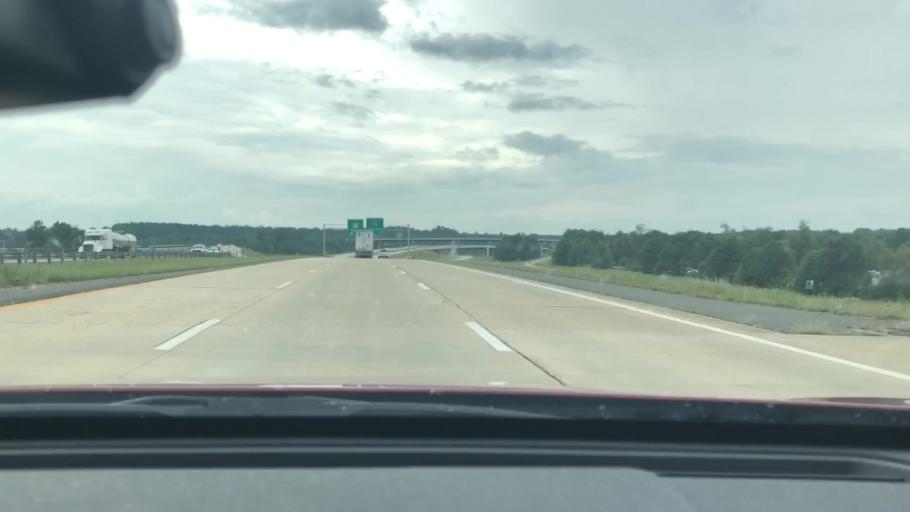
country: US
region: Texas
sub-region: Bowie County
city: Texarkana
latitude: 33.3935
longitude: -94.0139
